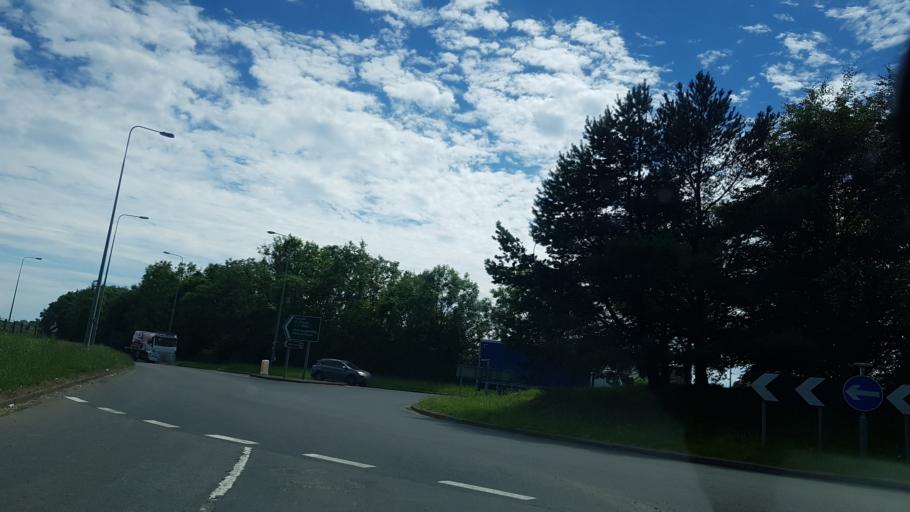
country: GB
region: Wales
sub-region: Pembrokeshire
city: Haverfordwest
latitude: 51.8161
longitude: -4.9568
